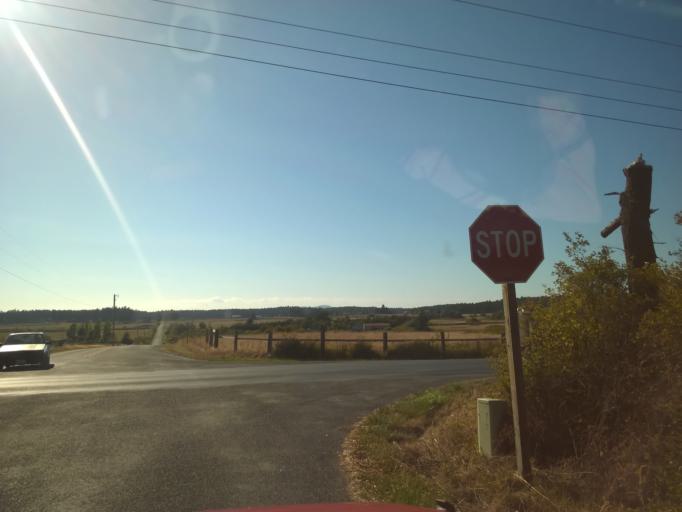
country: US
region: Washington
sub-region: San Juan County
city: Friday Harbor
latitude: 48.4782
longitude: -122.8990
